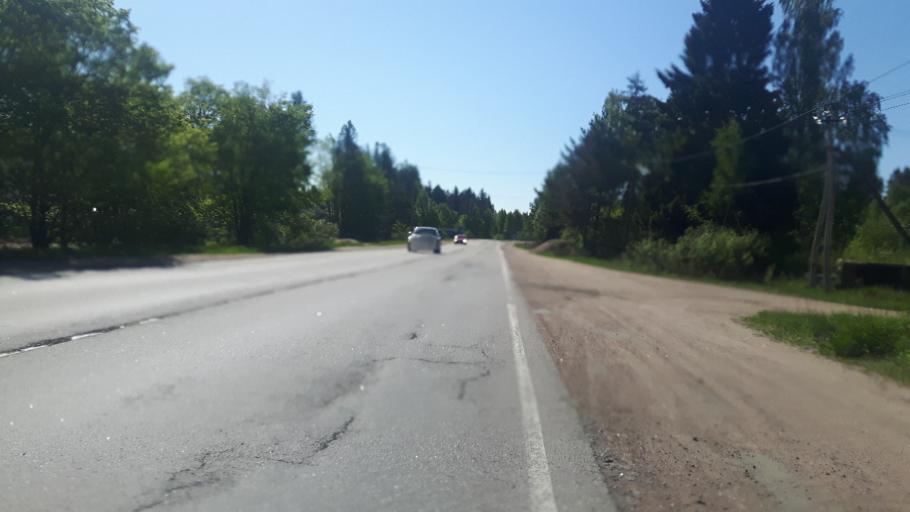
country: RU
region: Leningrad
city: Vyborg
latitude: 60.6506
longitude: 28.7465
